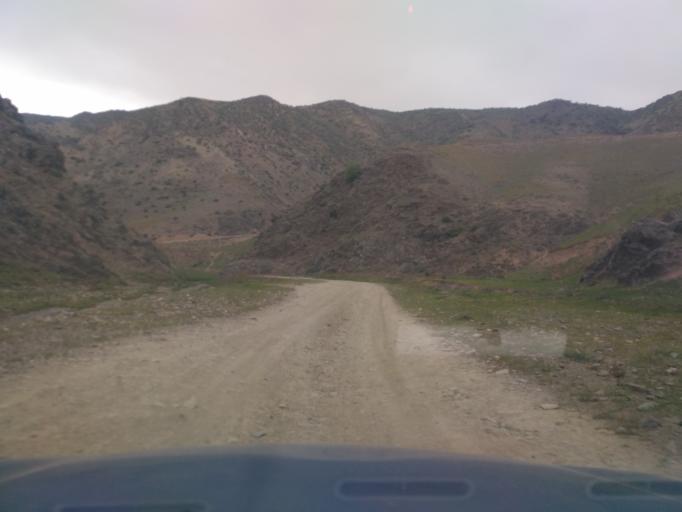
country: UZ
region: Jizzax
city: Zomin
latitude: 39.8560
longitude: 68.3895
